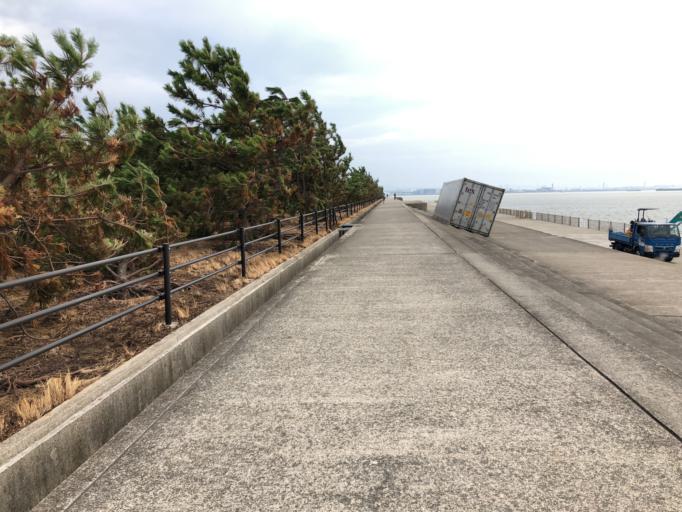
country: JP
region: Hyogo
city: Nishinomiya-hama
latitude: 34.7053
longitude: 135.3181
